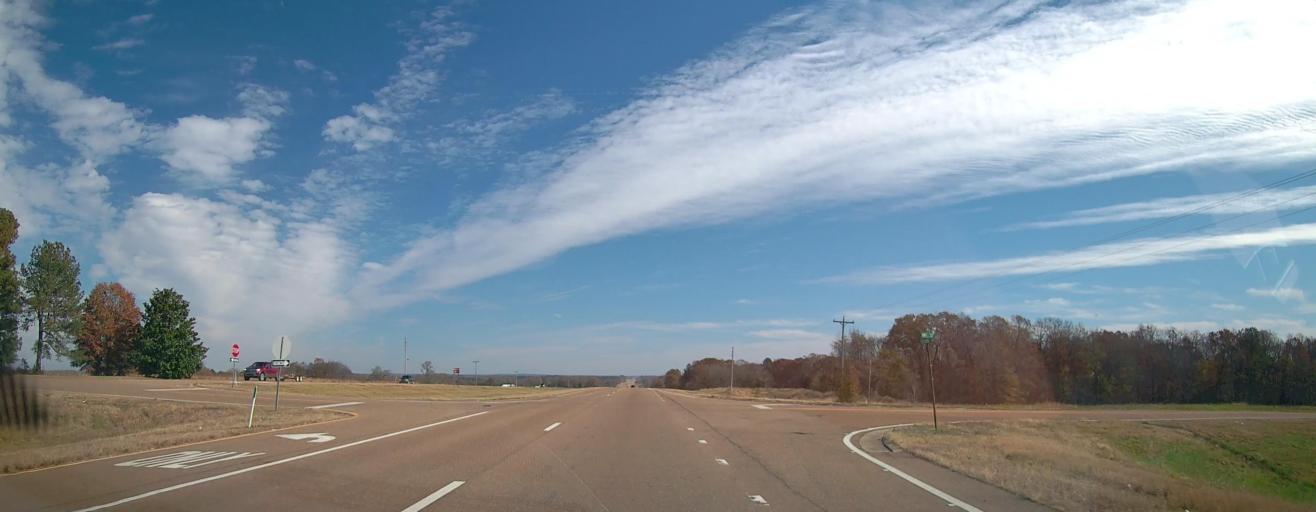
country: US
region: Mississippi
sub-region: Benton County
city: Ashland
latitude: 34.9461
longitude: -89.3180
